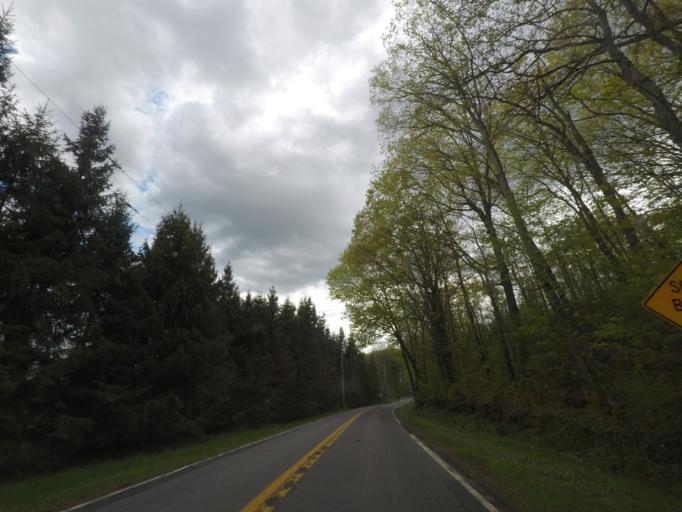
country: US
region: New York
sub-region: Albany County
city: Voorheesville
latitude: 42.6928
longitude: -73.9182
